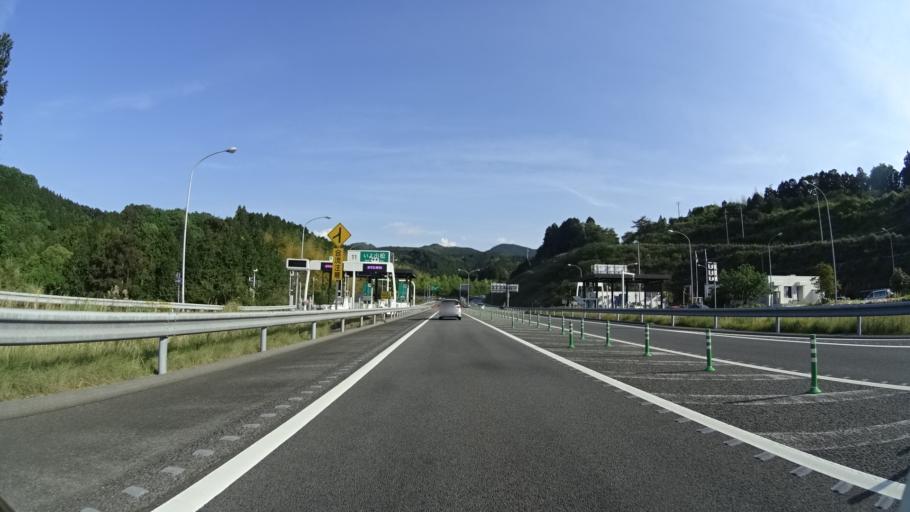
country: JP
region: Ehime
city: Saijo
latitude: 33.8863
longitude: 133.0876
